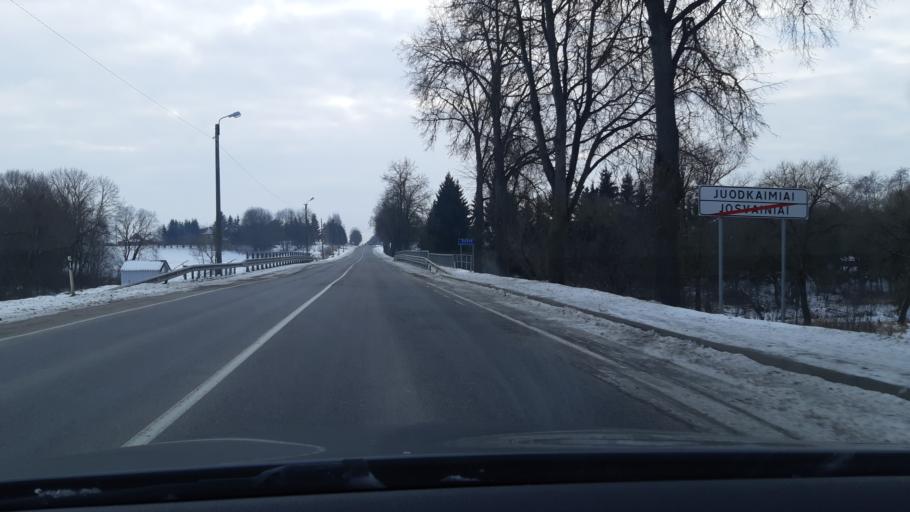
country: LT
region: Kauno apskritis
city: Kedainiai
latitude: 55.2429
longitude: 23.8335
